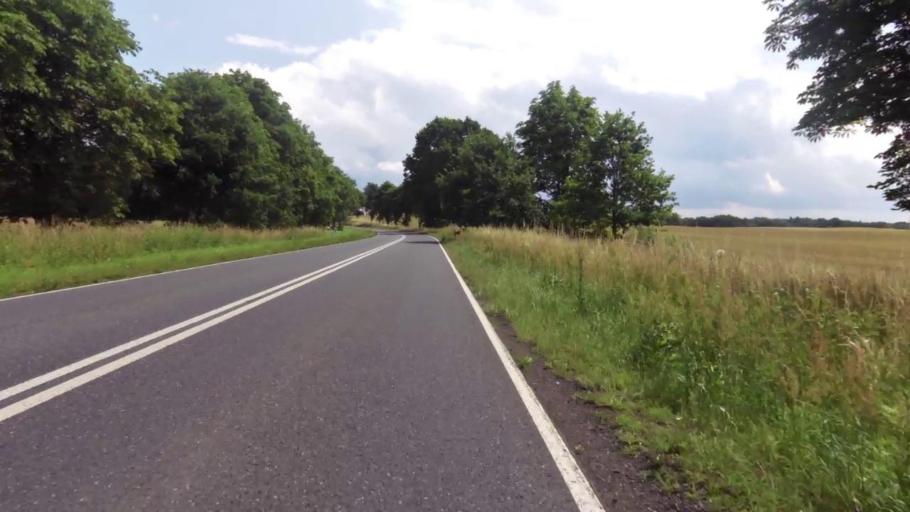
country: PL
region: West Pomeranian Voivodeship
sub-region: Powiat mysliborski
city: Nowogrodek Pomorski
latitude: 52.9948
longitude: 15.0830
